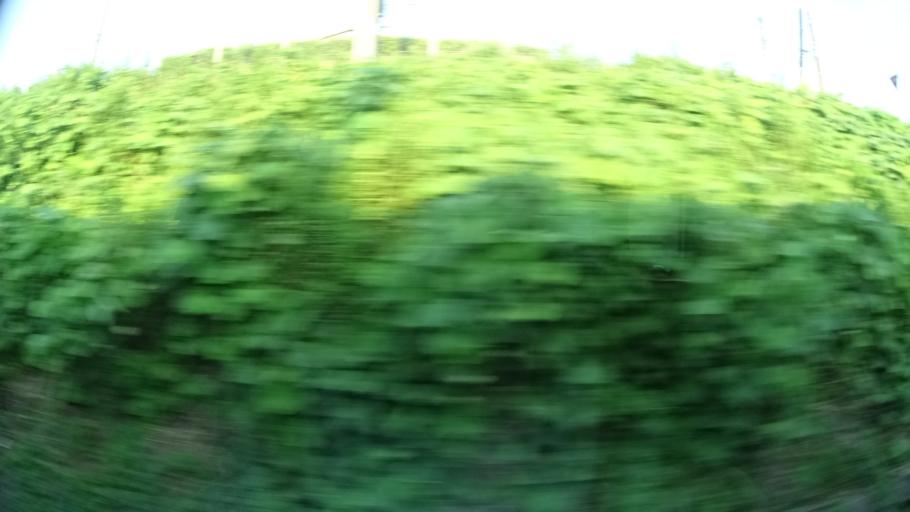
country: JP
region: Ibaraki
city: Tomobe
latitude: 36.3358
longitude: 140.2968
